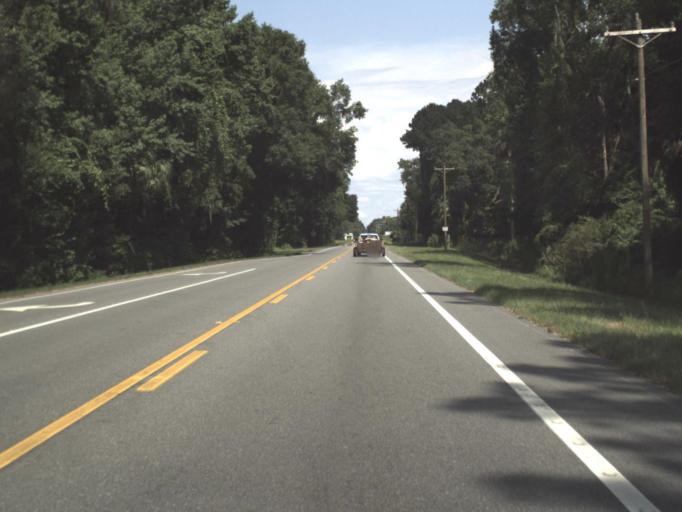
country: US
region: Florida
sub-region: Putnam County
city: Palatka
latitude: 29.6792
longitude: -81.7226
